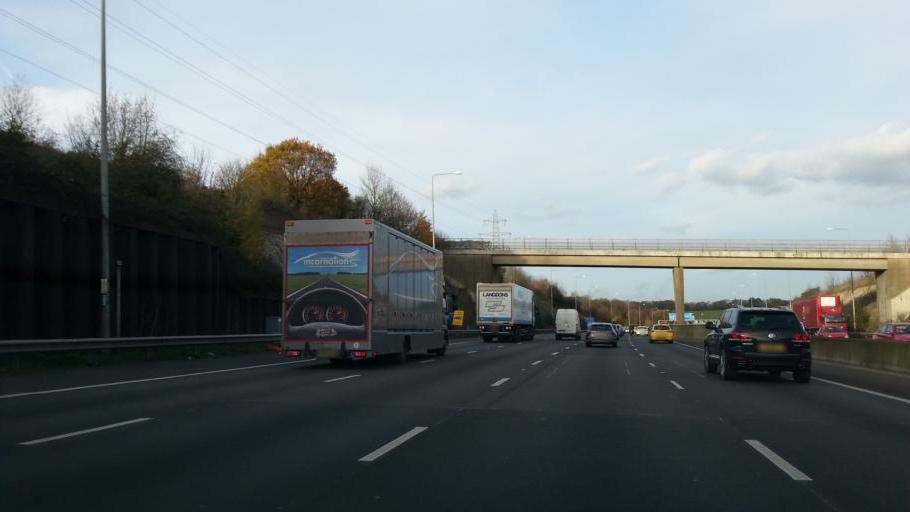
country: GB
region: England
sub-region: Buckinghamshire
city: Chalfont Saint Peter
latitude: 51.6222
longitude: -0.5249
